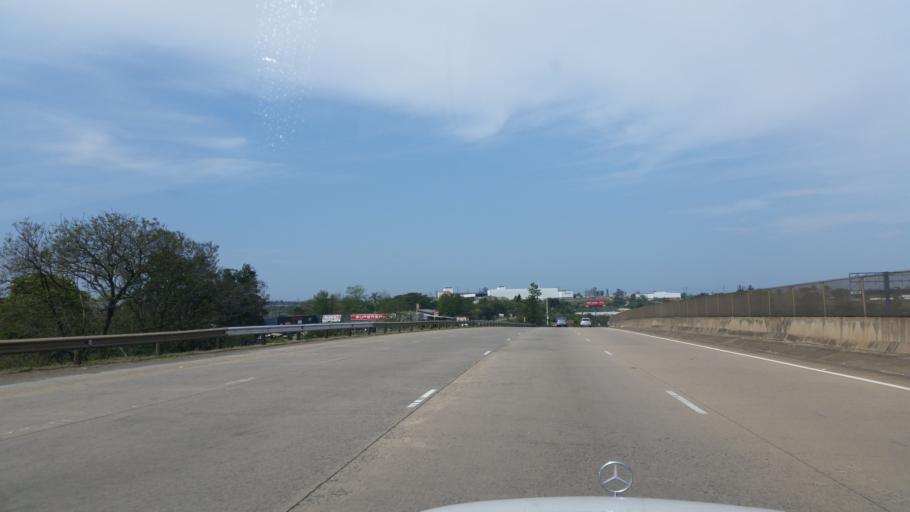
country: ZA
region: KwaZulu-Natal
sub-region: uMgungundlovu District Municipality
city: Camperdown
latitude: -29.7329
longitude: 30.5886
